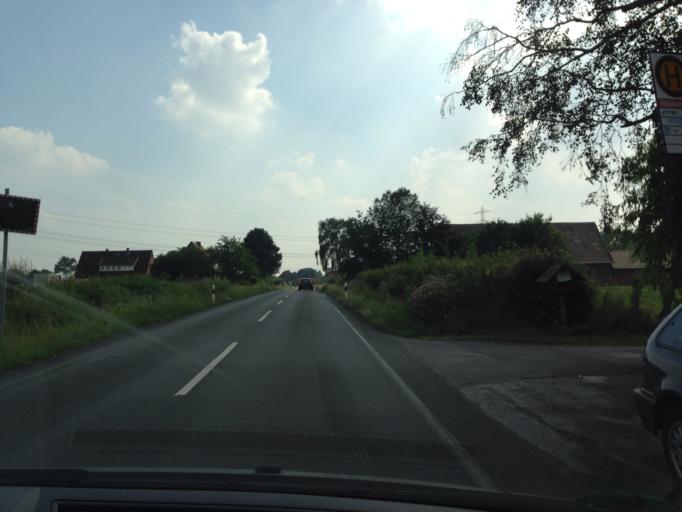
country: DE
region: North Rhine-Westphalia
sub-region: Regierungsbezirk Munster
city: Muenster
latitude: 51.9656
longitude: 7.5256
